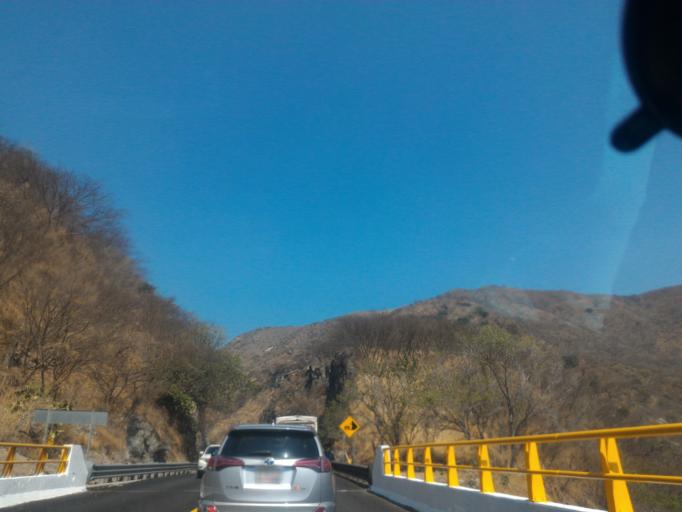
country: MX
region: Jalisco
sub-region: Tuxpan
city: La Higuera
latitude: 19.4971
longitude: -103.4434
